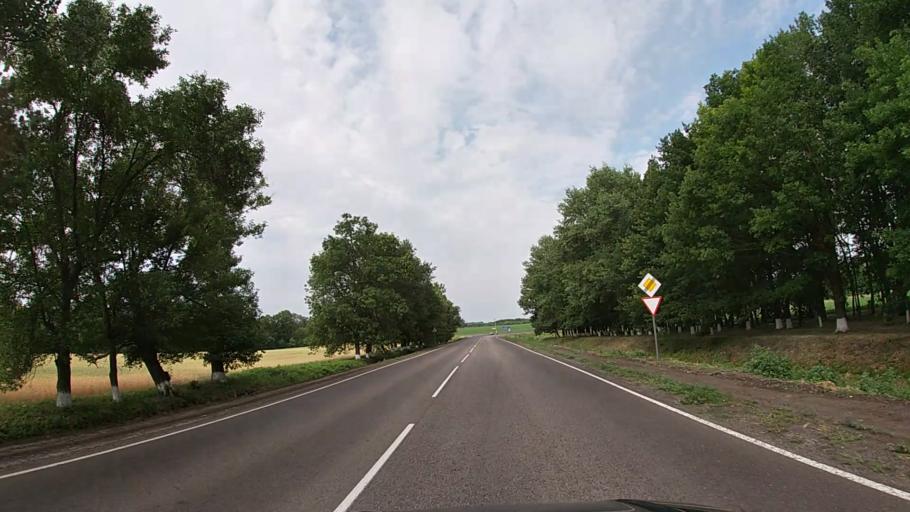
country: RU
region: Belgorod
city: Krasnaya Yaruga
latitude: 50.8095
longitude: 35.5031
